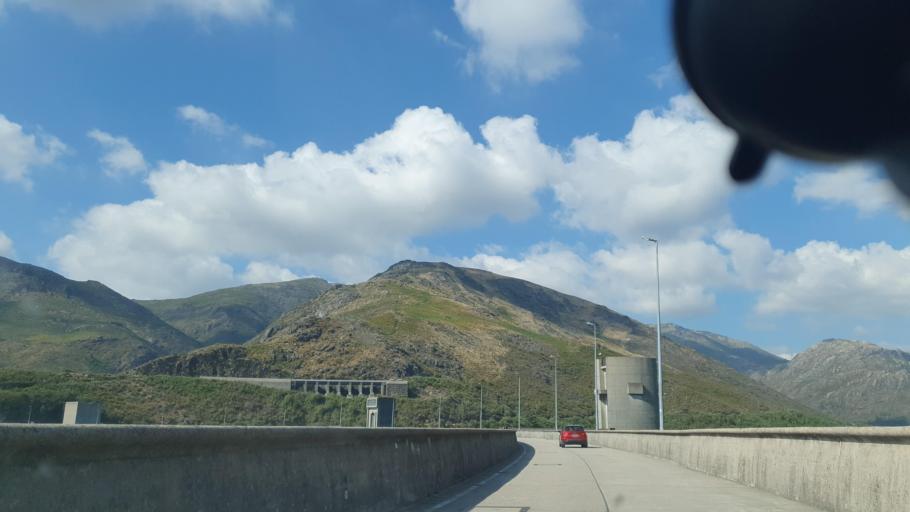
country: PT
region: Braga
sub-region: Terras de Bouro
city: Antas
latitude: 41.7620
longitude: -8.2087
